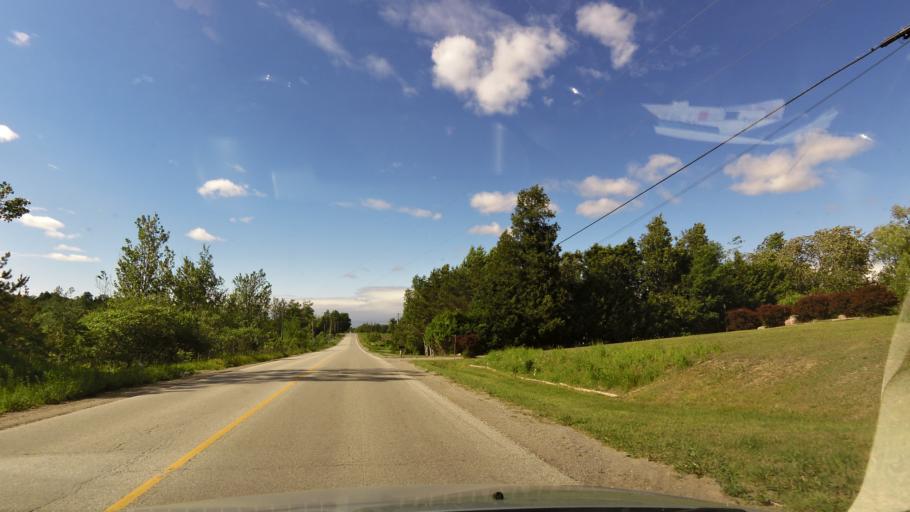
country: CA
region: Ontario
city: Bradford West Gwillimbury
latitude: 44.1757
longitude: -79.6189
